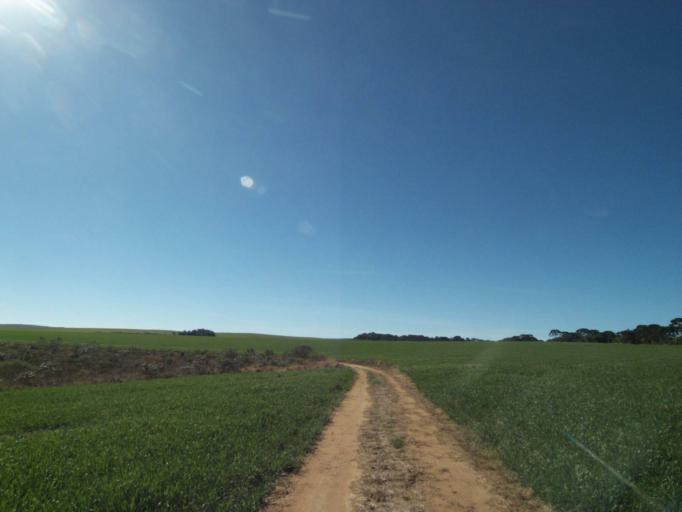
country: BR
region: Parana
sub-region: Tibagi
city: Tibagi
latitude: -24.5926
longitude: -50.2504
